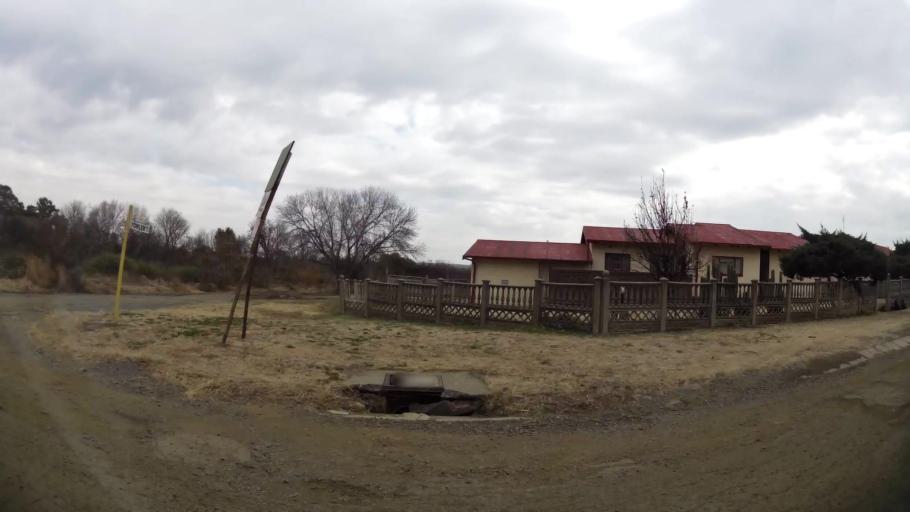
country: ZA
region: Orange Free State
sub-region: Fezile Dabi District Municipality
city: Kroonstad
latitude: -27.6848
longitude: 27.2280
